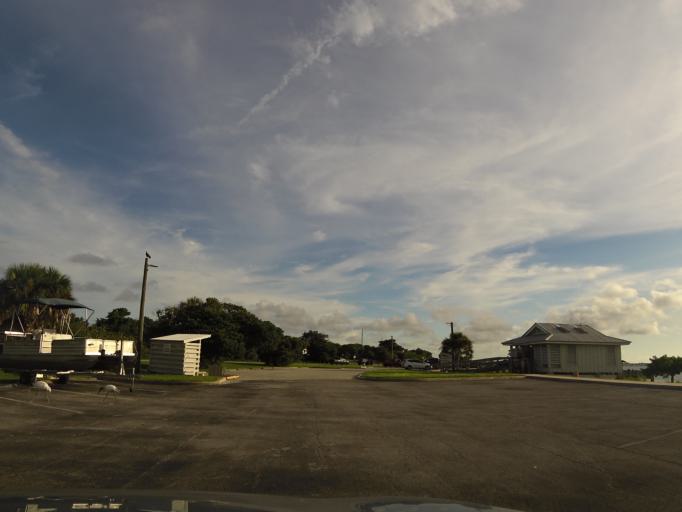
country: US
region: Florida
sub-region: Indian River County
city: Sebastian
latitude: 27.8558
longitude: -80.4513
